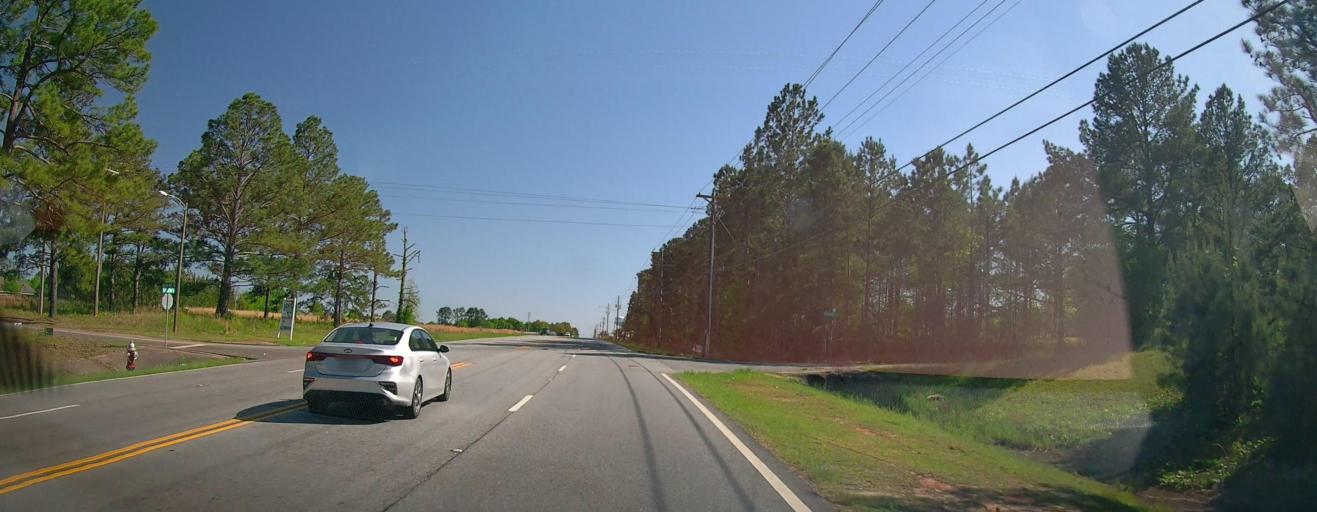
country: US
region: Georgia
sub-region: Houston County
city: Warner Robins
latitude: 32.6481
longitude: -83.6414
